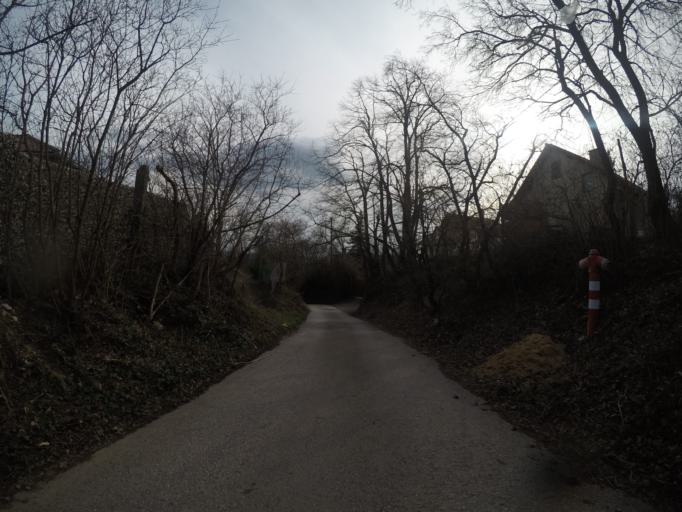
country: HU
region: Baranya
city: Pecs
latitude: 46.0895
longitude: 18.2009
